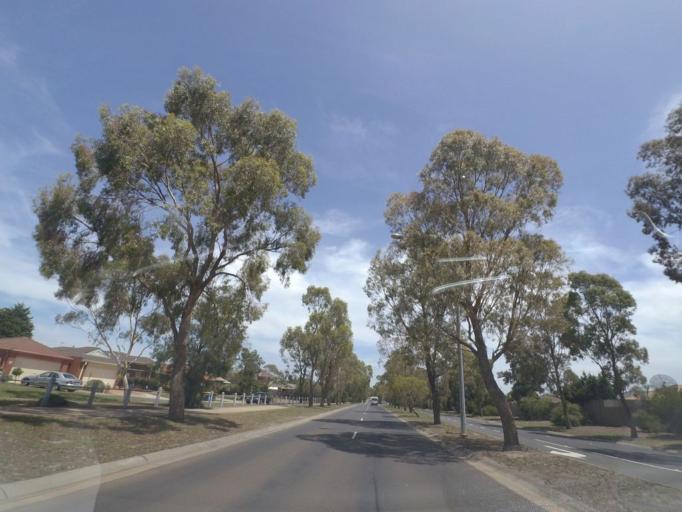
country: AU
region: Victoria
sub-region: Hume
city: Roxburgh Park
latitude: -37.6313
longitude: 144.9257
